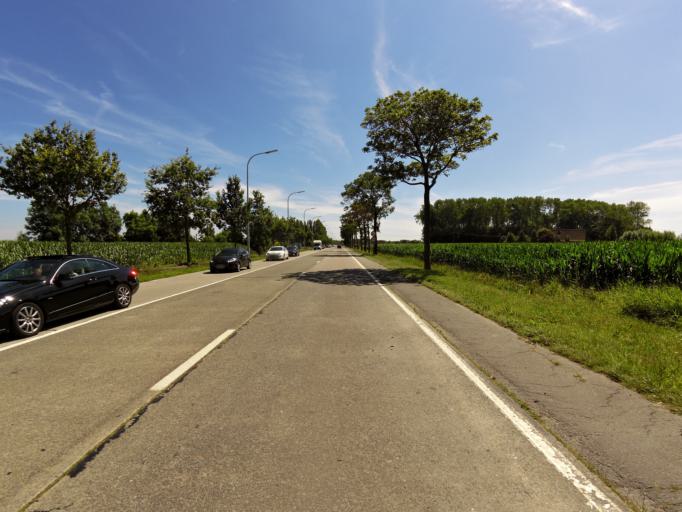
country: BE
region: Flanders
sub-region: Provincie West-Vlaanderen
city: Zuienkerke
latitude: 51.2768
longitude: 3.1728
